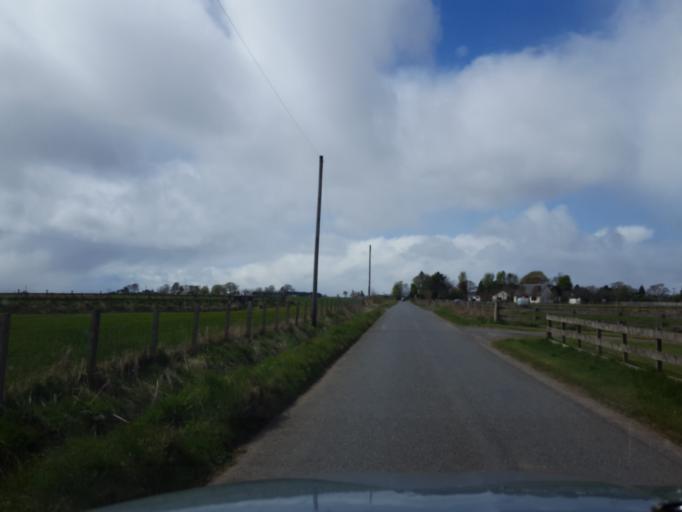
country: GB
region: Scotland
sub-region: Perth and Kinross
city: Scone
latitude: 56.4379
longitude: -3.3523
